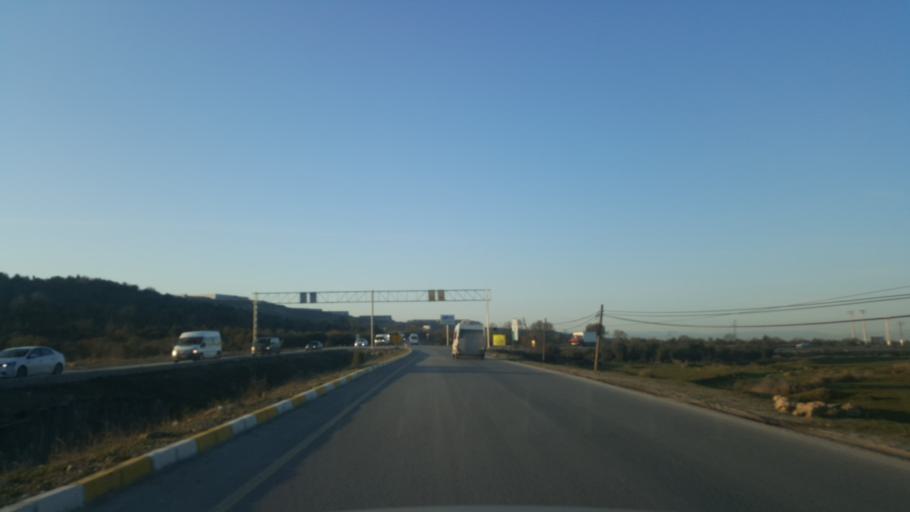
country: TR
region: Kocaeli
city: Tavsanli
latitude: 40.8562
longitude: 29.5562
